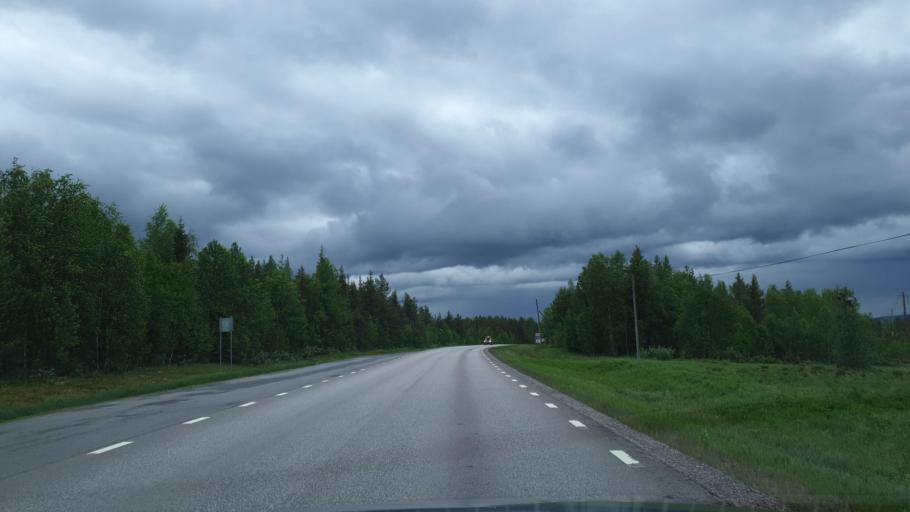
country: SE
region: Norrbotten
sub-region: Gallivare Kommun
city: Malmberget
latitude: 67.4488
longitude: 21.1215
